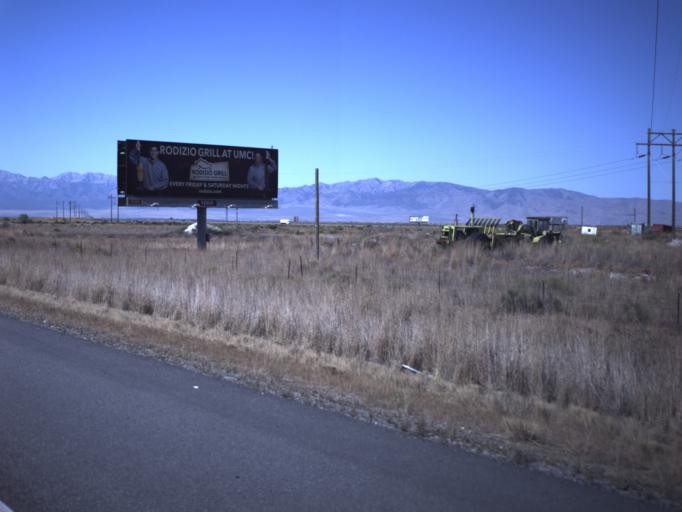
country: US
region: Utah
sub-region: Tooele County
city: Stansbury park
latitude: 40.6810
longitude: -112.2729
